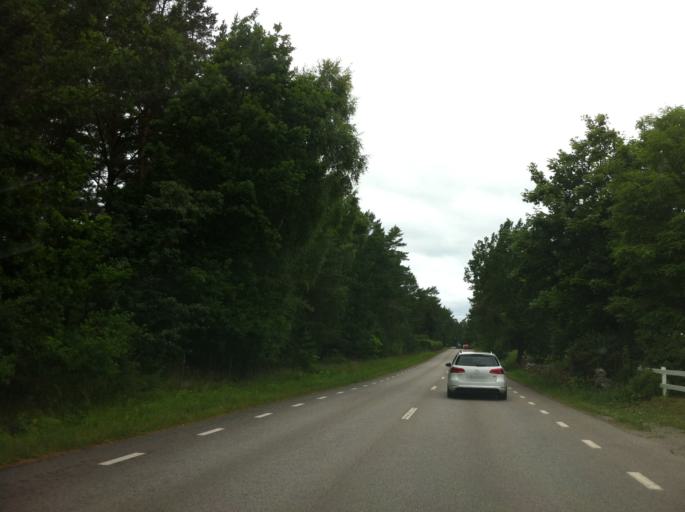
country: SE
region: Kalmar
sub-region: Borgholms Kommun
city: Borgholm
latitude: 57.2548
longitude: 17.0509
